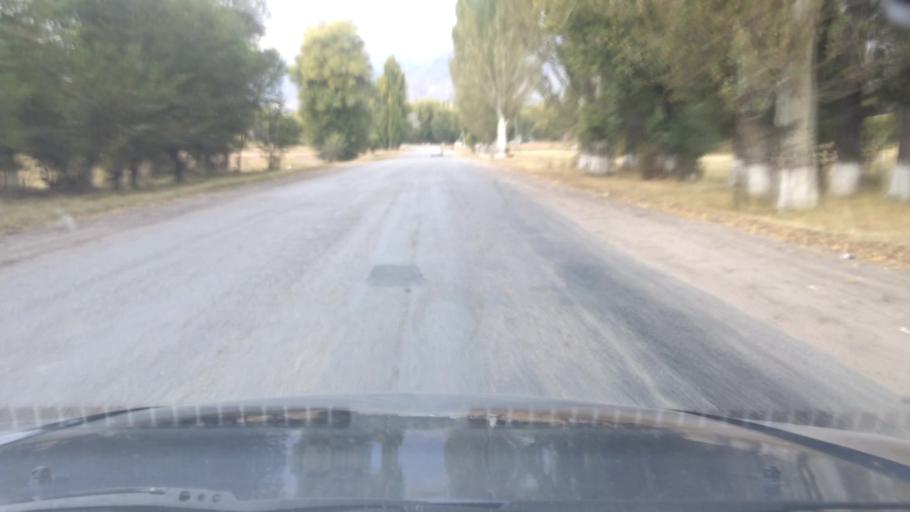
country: KG
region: Ysyk-Koel
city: Tyup
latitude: 42.7861
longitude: 78.2669
